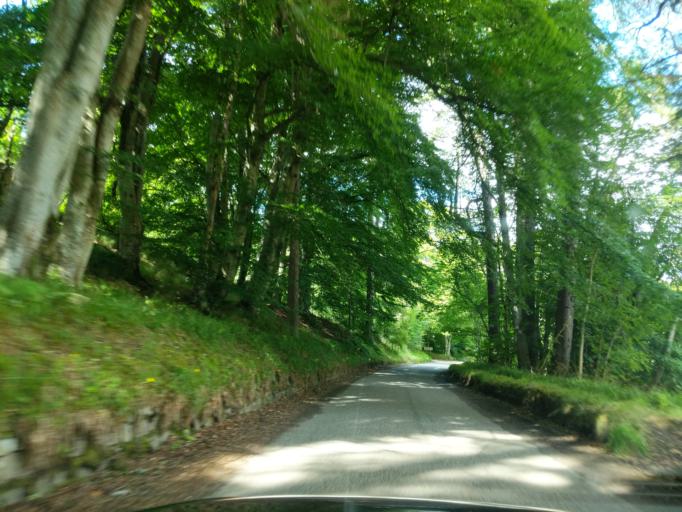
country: GB
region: Scotland
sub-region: Aberdeenshire
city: Ballater
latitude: 57.0330
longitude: -3.2110
